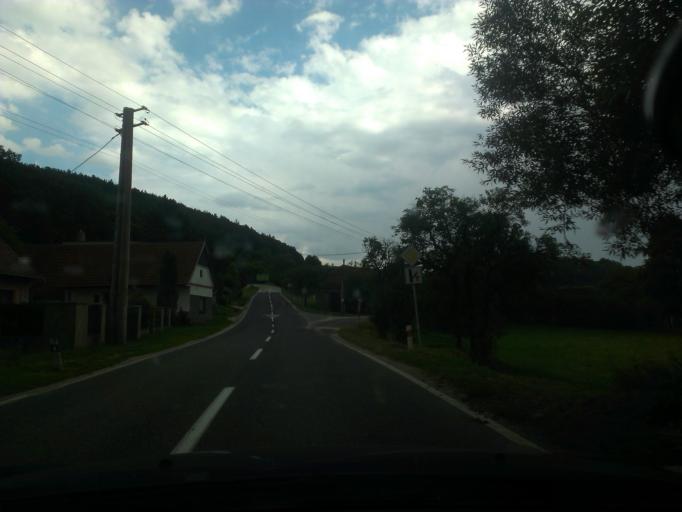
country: CZ
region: South Moravian
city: Velka nad Velickou
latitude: 48.8138
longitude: 17.5174
